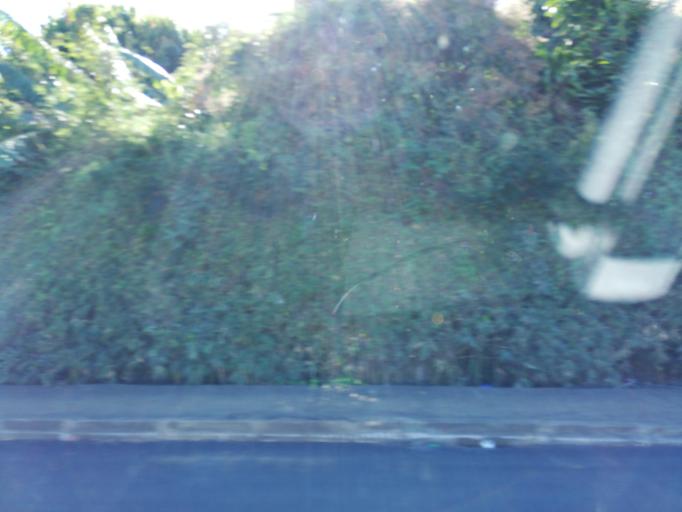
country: MU
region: Plaines Wilhems
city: Ebene
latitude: -20.2342
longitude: 57.4724
